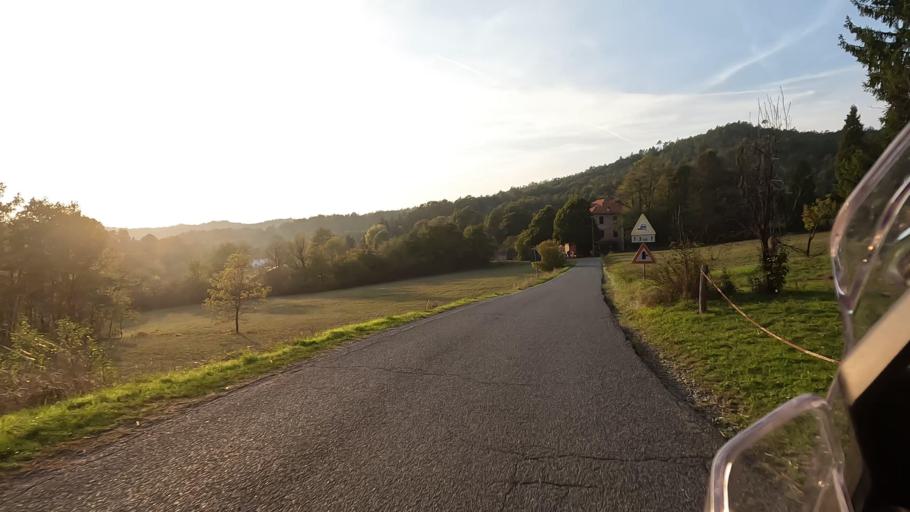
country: IT
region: Liguria
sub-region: Provincia di Savona
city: Mioglia
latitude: 44.5136
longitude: 8.4508
